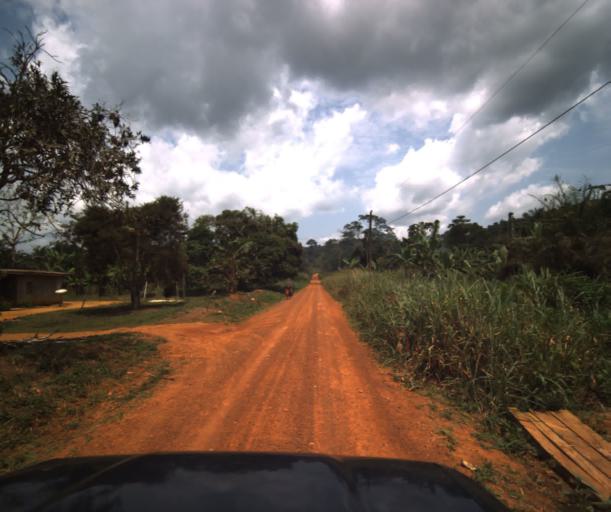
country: CM
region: Centre
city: Eseka
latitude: 3.5509
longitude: 10.9200
